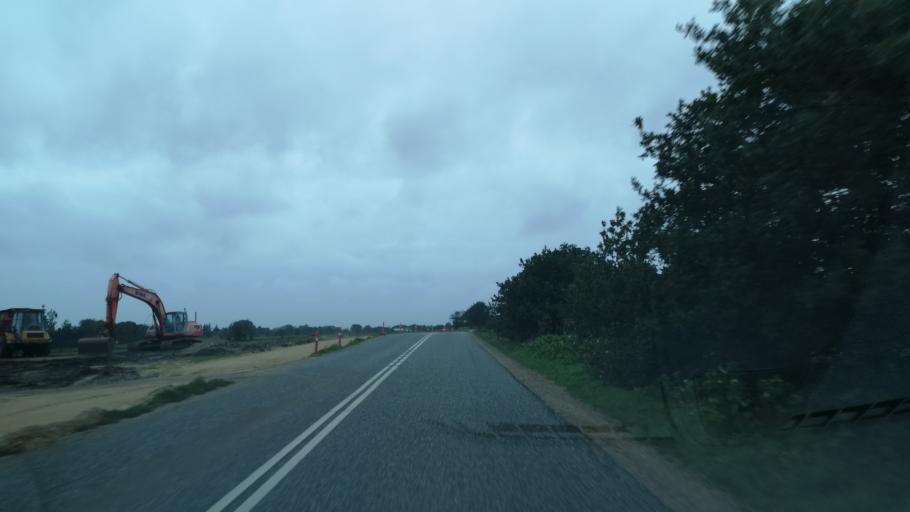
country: DK
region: Central Jutland
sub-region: Ringkobing-Skjern Kommune
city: Videbaek
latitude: 56.0541
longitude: 8.6391
